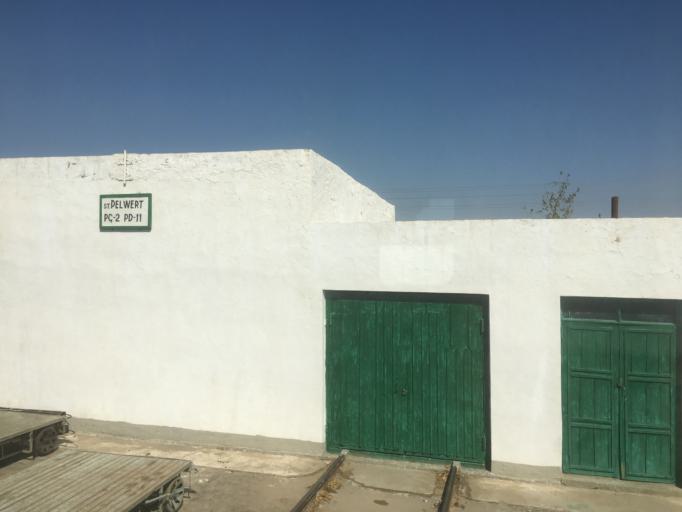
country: TM
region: Lebap
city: Atamyrat
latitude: 38.1893
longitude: 64.5147
